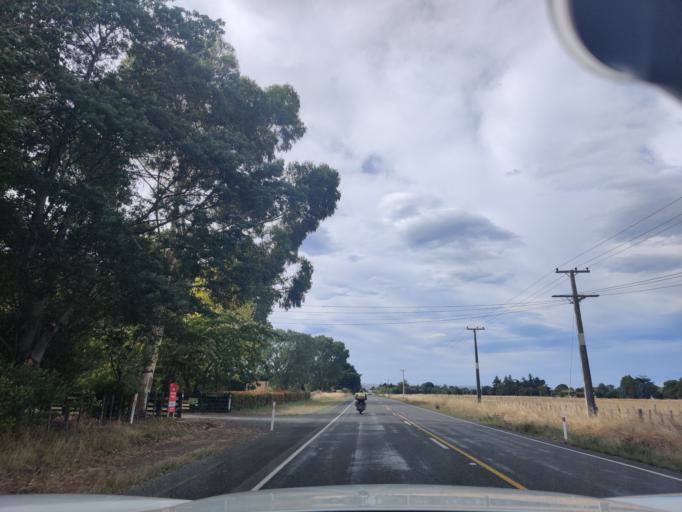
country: NZ
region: Wellington
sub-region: Masterton District
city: Masterton
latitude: -40.8848
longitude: 175.6590
